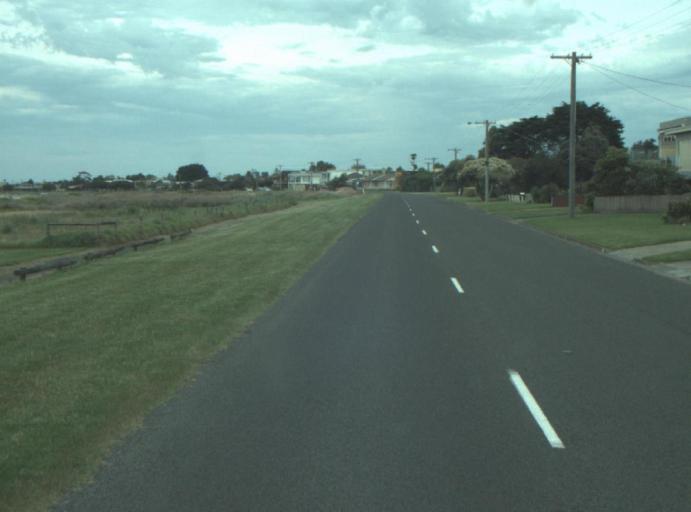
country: AU
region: Victoria
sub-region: Greater Geelong
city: Clifton Springs
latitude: -38.1245
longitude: 144.6955
